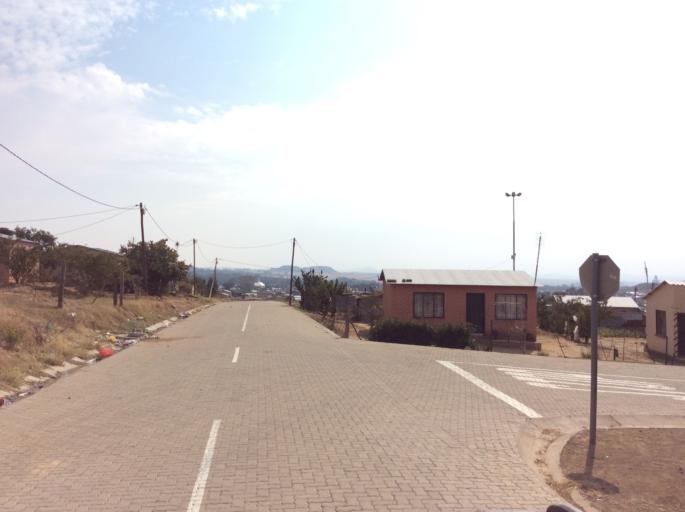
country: ZA
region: Orange Free State
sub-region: Xhariep District Municipality
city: Dewetsdorp
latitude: -29.5937
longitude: 26.6774
